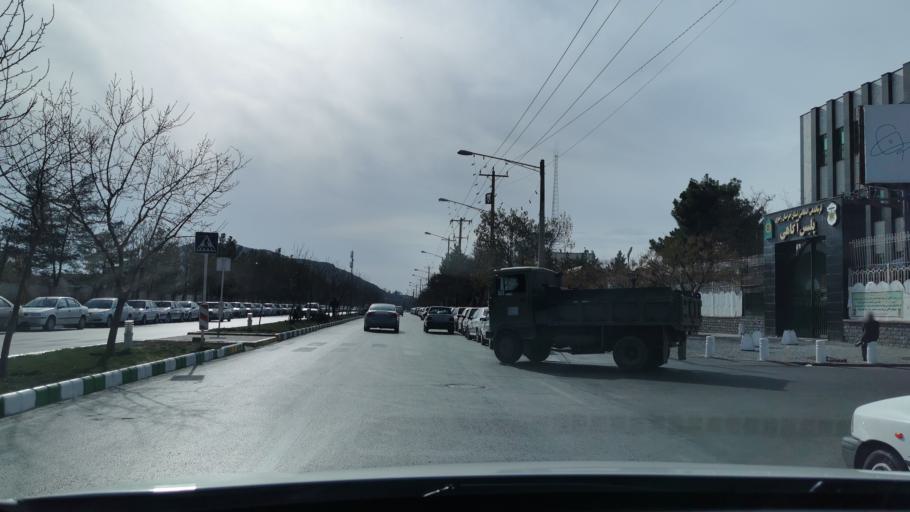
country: IR
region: Razavi Khorasan
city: Mashhad
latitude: 36.2825
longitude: 59.5514
